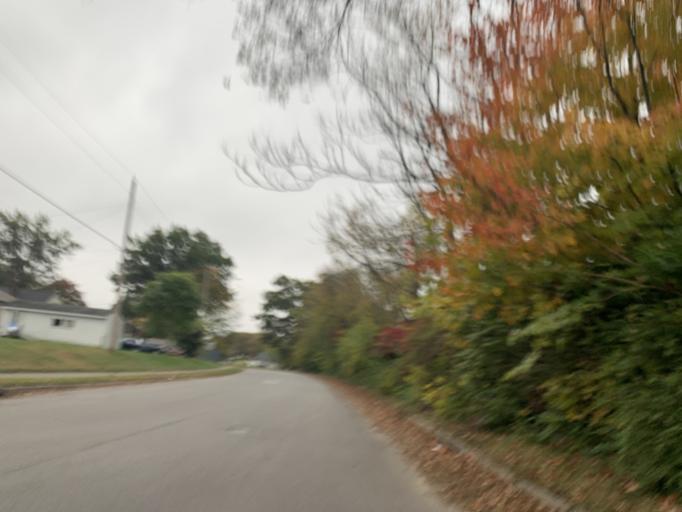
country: US
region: Indiana
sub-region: Floyd County
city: New Albany
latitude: 38.2521
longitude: -85.8058
